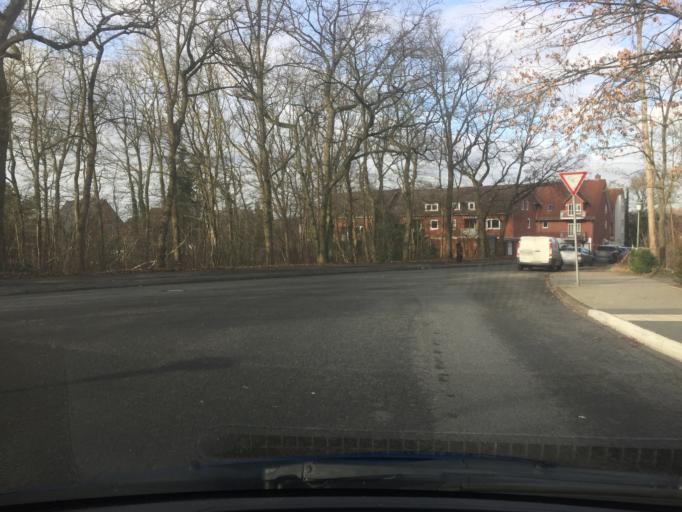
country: DE
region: Lower Saxony
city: Lueneburg
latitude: 53.2360
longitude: 10.4297
